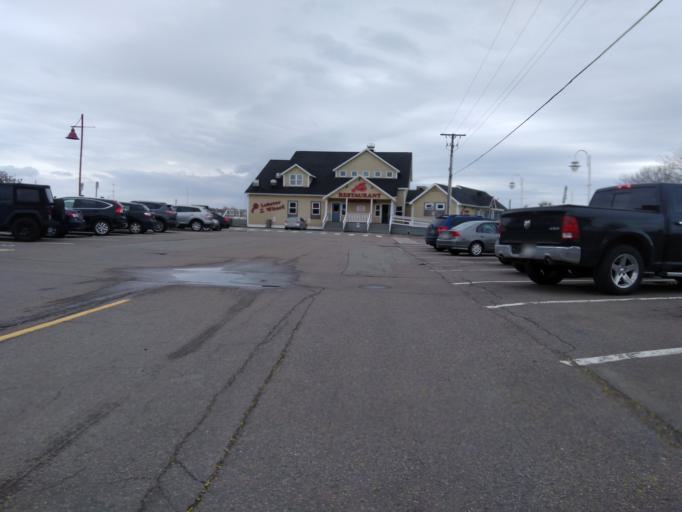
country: CA
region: Prince Edward Island
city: Charlottetown
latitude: 46.2331
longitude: -63.1208
